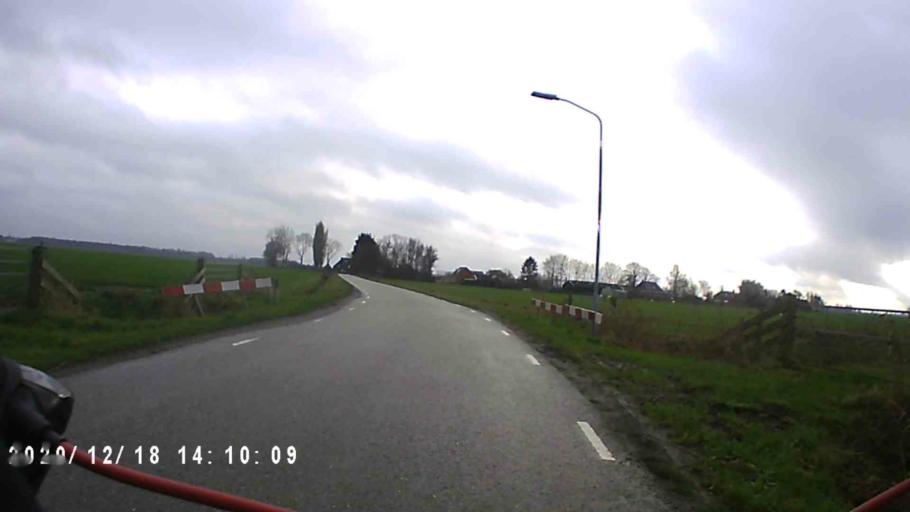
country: NL
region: Groningen
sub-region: Gemeente Bedum
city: Bedum
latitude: 53.2776
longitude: 6.6593
